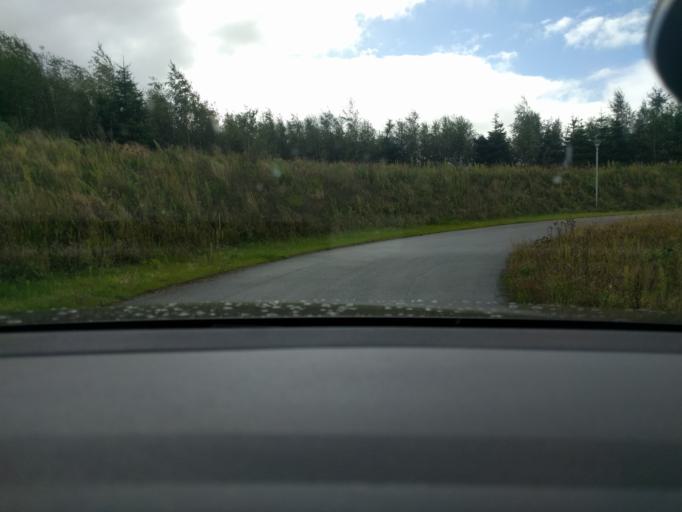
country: DK
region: Central Jutland
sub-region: Viborg Kommune
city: Viborg
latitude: 56.4241
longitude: 9.4134
